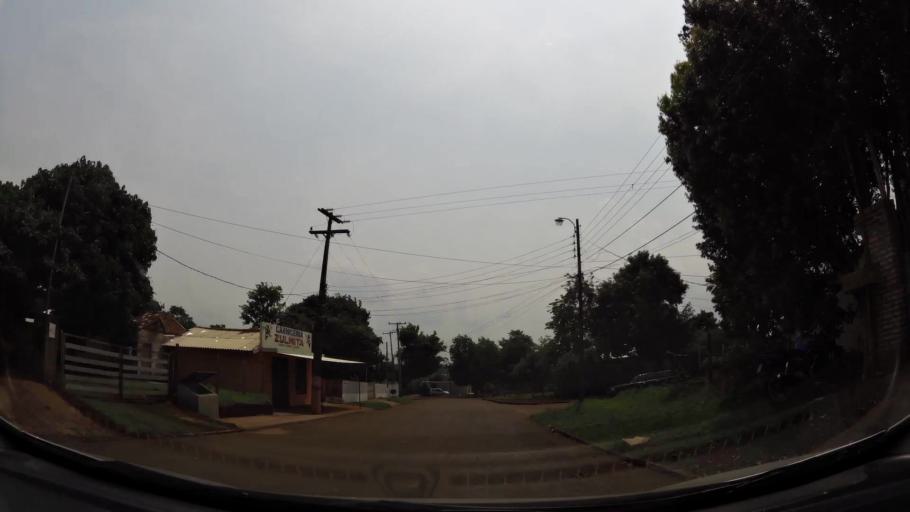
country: BR
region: Parana
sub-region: Foz Do Iguacu
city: Foz do Iguacu
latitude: -25.5709
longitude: -54.6147
